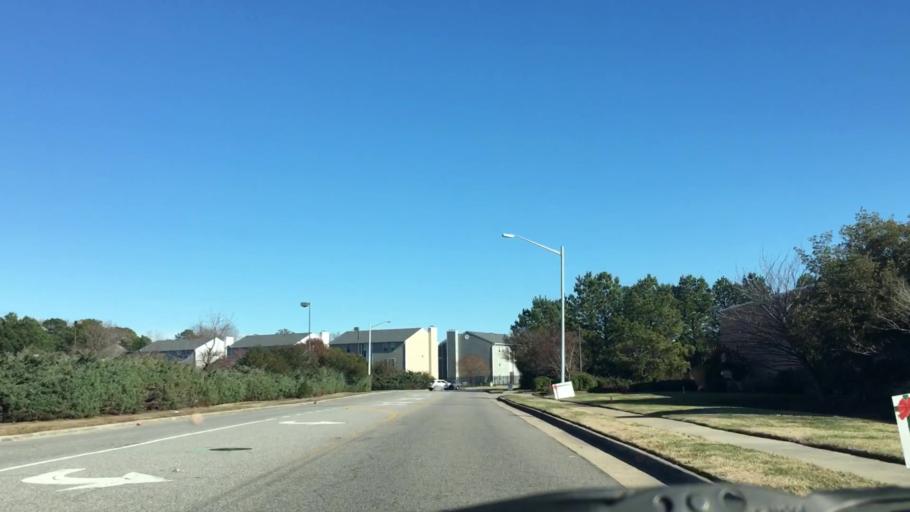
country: US
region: Virginia
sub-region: City of Virginia Beach
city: Virginia Beach
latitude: 36.8511
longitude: -76.0271
